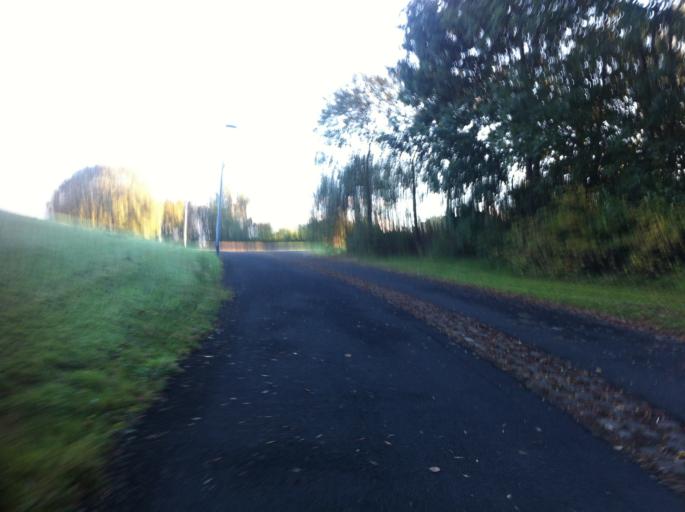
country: GB
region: Scotland
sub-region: Glasgow City
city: Glasgow
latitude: 55.8700
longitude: -4.2440
